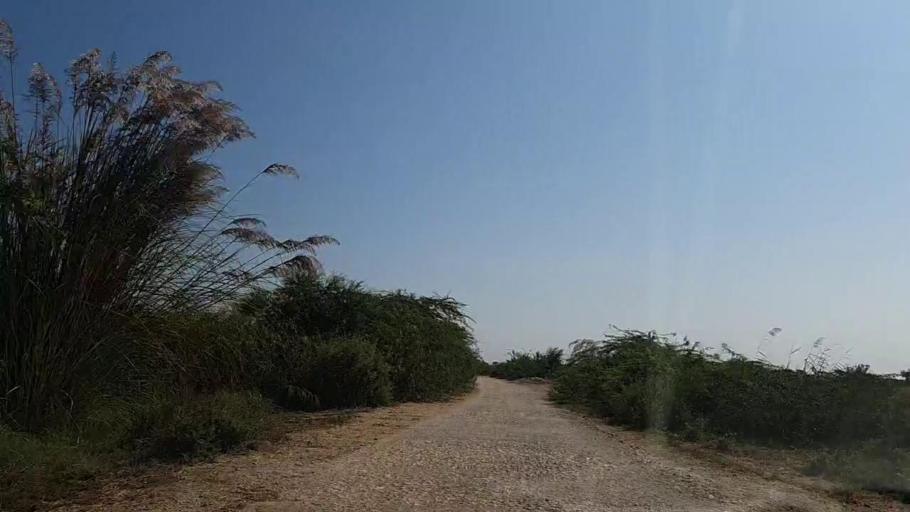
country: PK
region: Sindh
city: Chuhar Jamali
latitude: 24.4619
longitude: 68.1073
